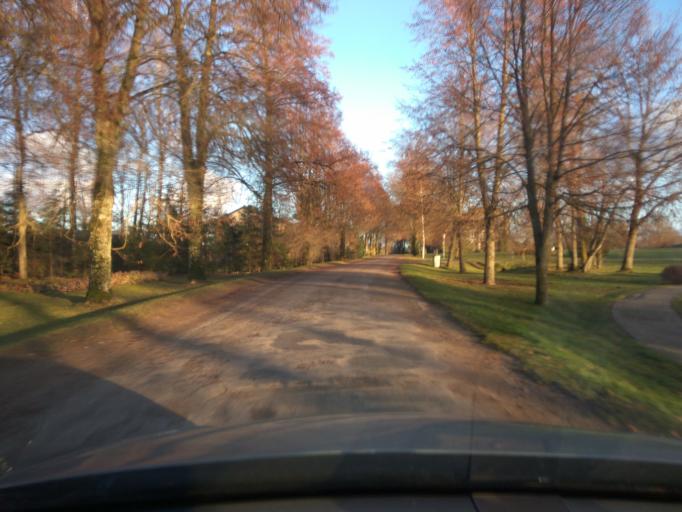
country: LV
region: Aizpute
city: Aizpute
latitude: 56.8362
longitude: 21.7709
